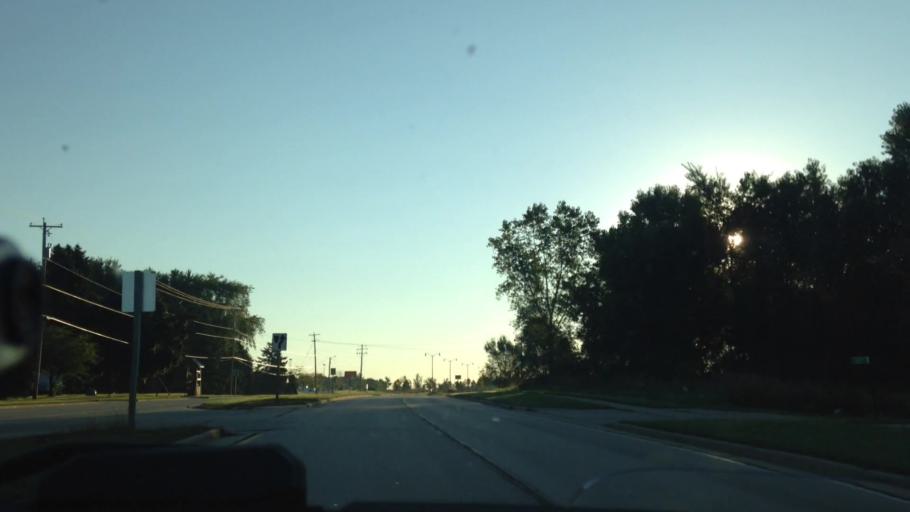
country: US
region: Wisconsin
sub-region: Ozaukee County
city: Saukville
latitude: 43.3867
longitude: -87.9135
